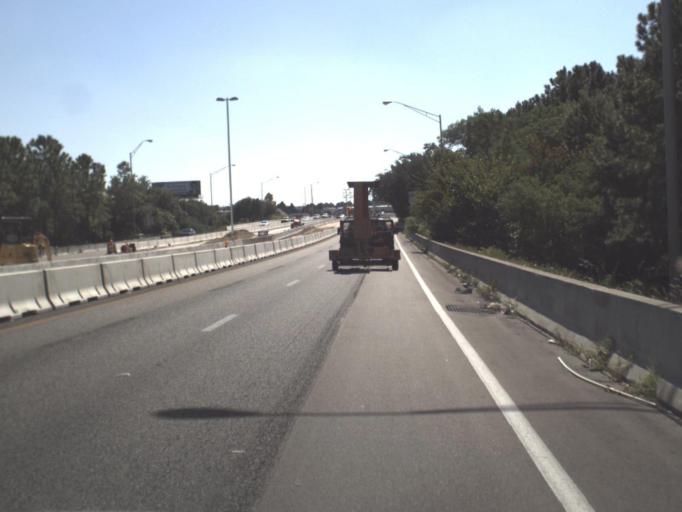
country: US
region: Florida
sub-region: Hillsborough County
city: Town 'n' Country
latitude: 28.0055
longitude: -82.5456
